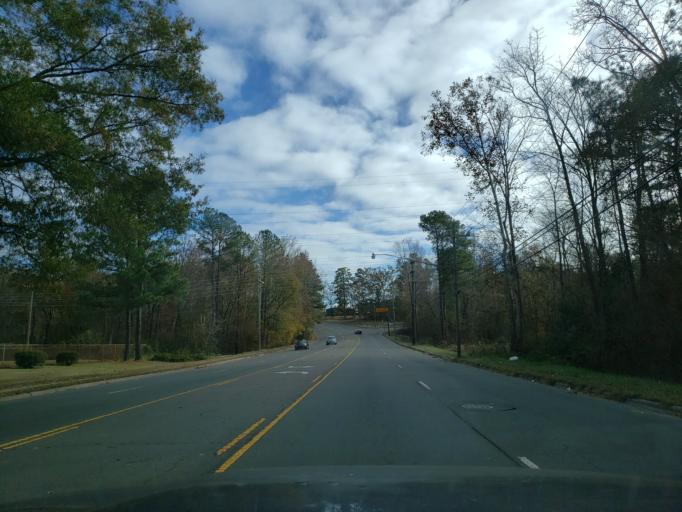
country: US
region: North Carolina
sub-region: Durham County
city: Durham
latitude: 35.9623
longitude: -78.9159
